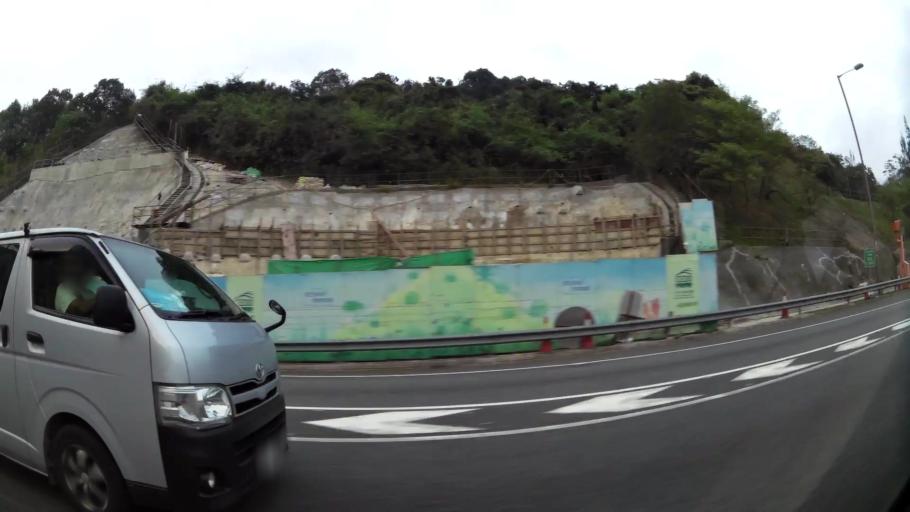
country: HK
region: Sha Tin
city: Sha Tin
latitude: 22.3900
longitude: 114.2105
